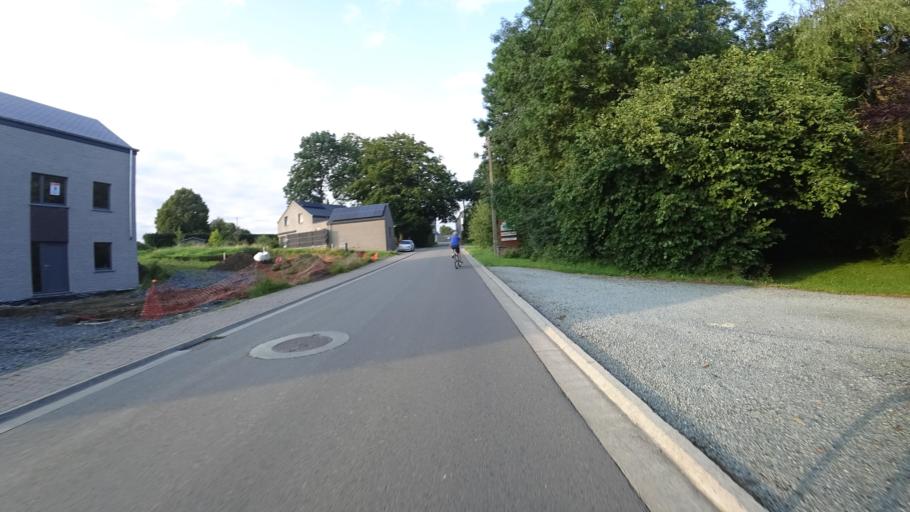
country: BE
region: Wallonia
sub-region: Province du Luxembourg
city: Neufchateau
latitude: 49.9027
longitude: 5.3866
